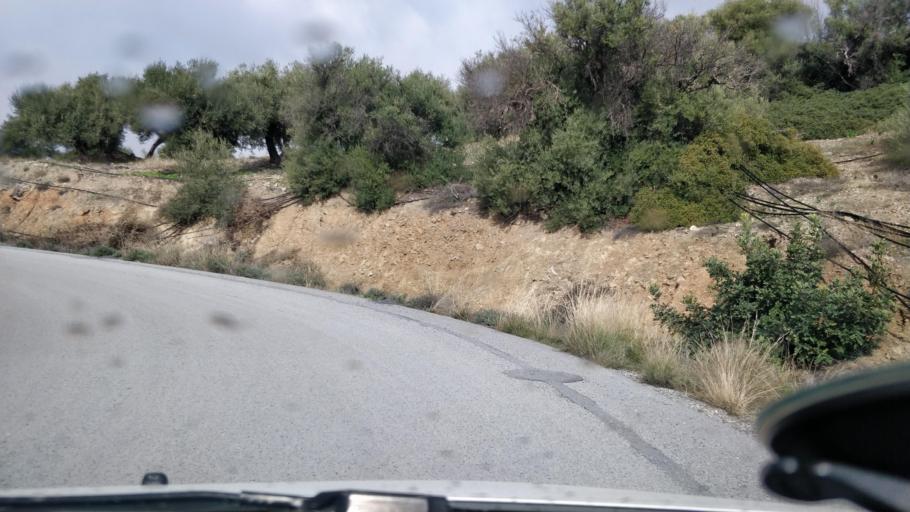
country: GR
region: Crete
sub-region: Nomos Lasithiou
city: Gra Liyia
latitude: 34.9971
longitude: 25.5126
